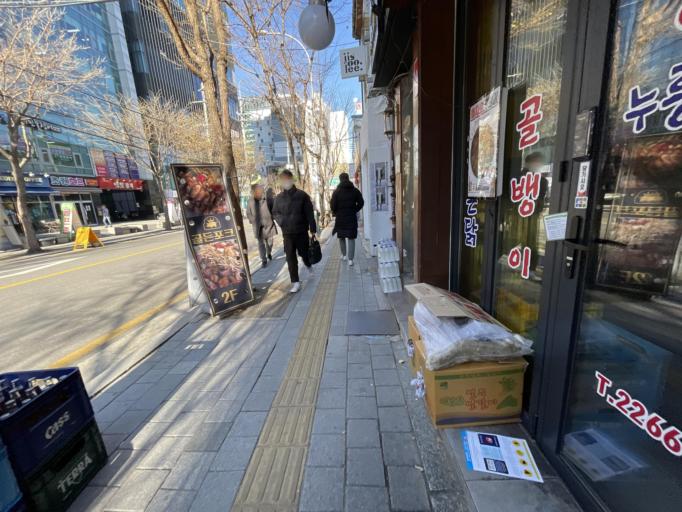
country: KR
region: Seoul
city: Seoul
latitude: 37.5652
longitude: 126.9899
